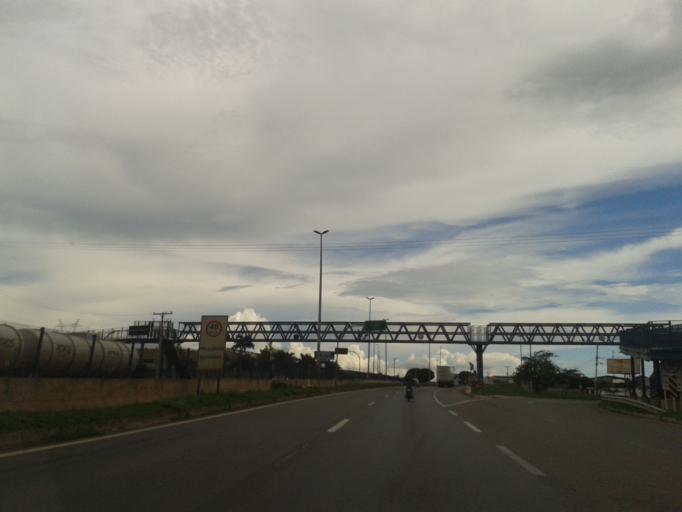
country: BR
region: Goias
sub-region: Aparecida De Goiania
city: Aparecida de Goiania
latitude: -16.8099
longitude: -49.2396
